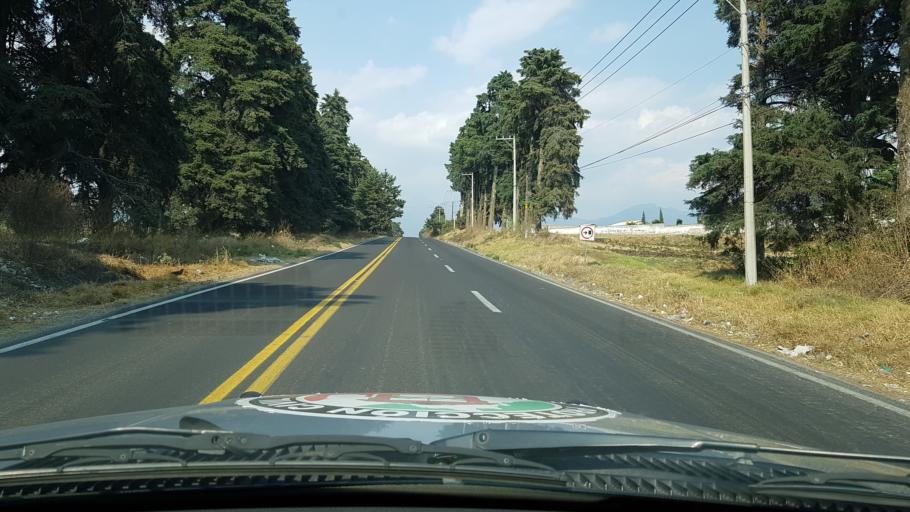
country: MX
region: Mexico
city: Ozumba de Alzate
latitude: 19.0398
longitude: -98.8048
